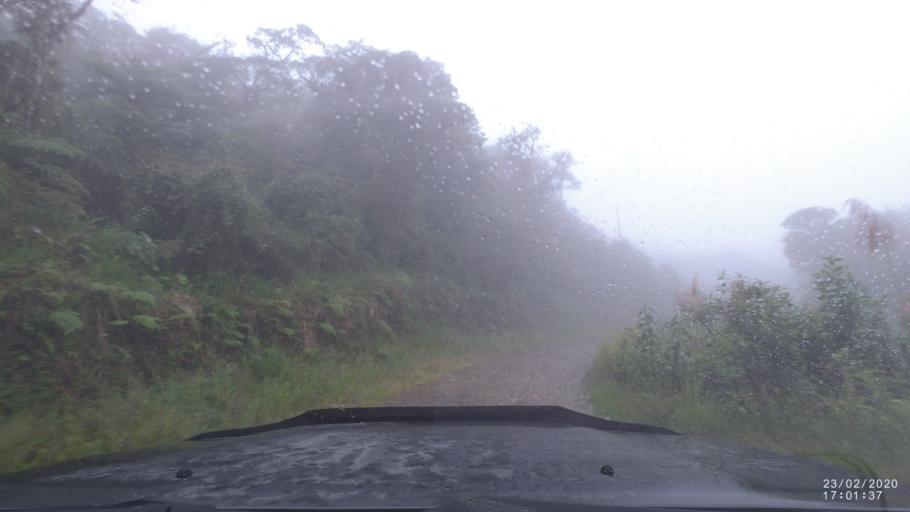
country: BO
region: Cochabamba
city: Colomi
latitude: -17.1125
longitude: -65.9651
